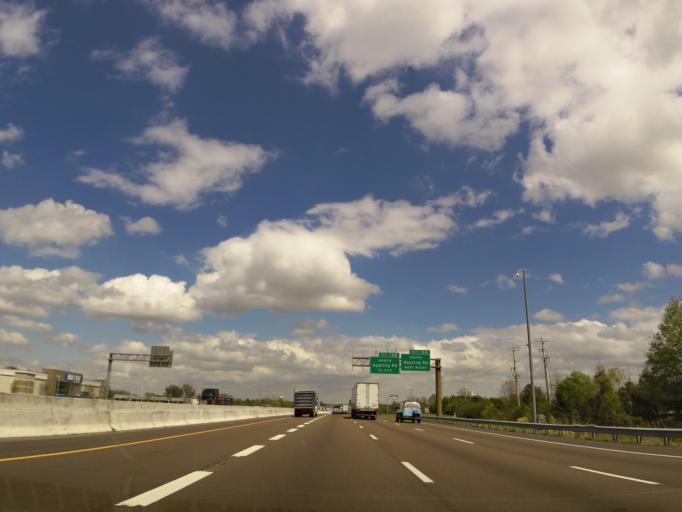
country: US
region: Tennessee
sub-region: Shelby County
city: Bartlett
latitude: 35.1809
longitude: -89.8234
